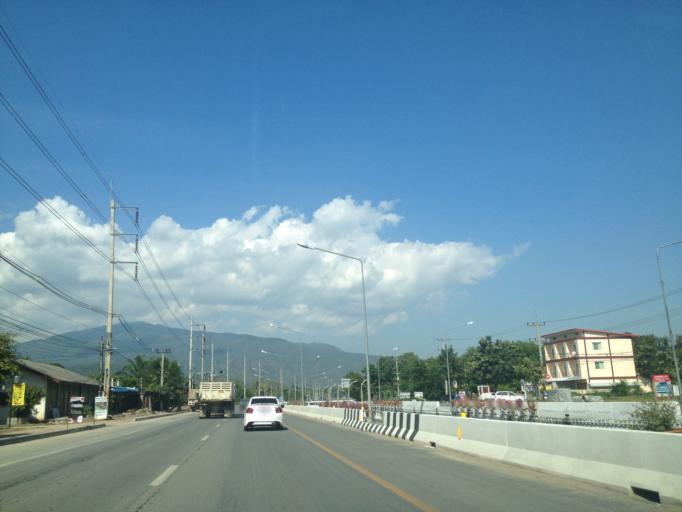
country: TH
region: Chiang Mai
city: Hang Dong
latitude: 18.7264
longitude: 98.9266
